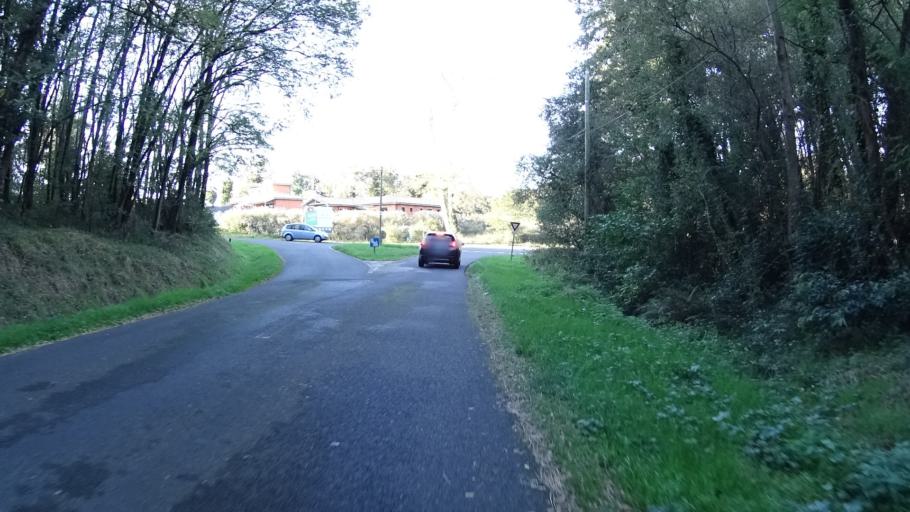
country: FR
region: Aquitaine
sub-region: Departement des Landes
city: Saint-Paul-les-Dax
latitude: 43.7378
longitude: -1.0436
